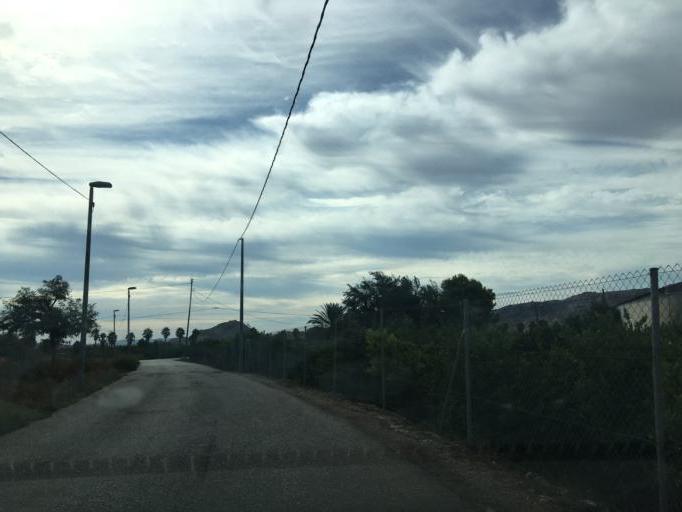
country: ES
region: Murcia
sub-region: Murcia
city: Santomera
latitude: 38.0116
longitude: -1.0423
